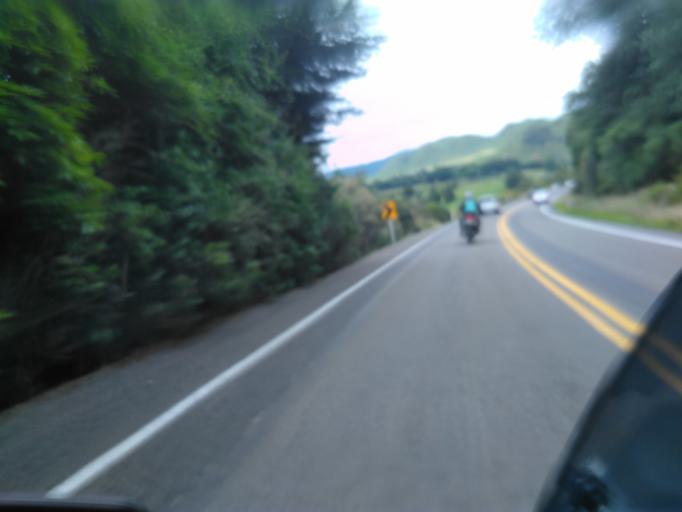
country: NZ
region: Bay of Plenty
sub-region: Opotiki District
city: Opotiki
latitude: -38.3638
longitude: 177.4906
